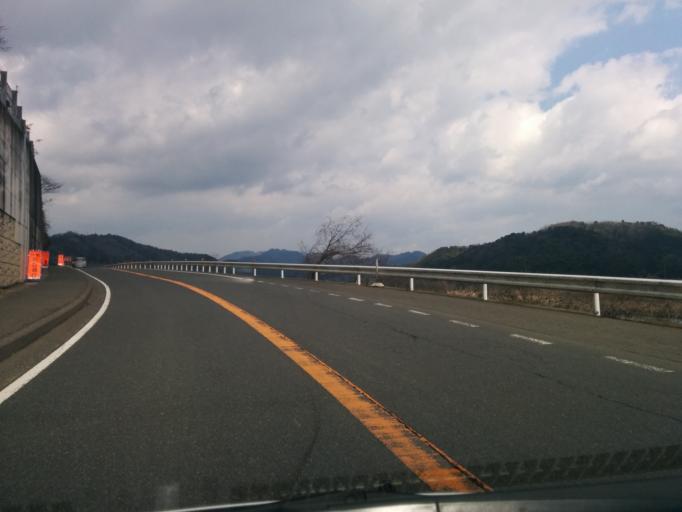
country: JP
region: Kyoto
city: Maizuru
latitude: 35.4424
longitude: 135.2582
